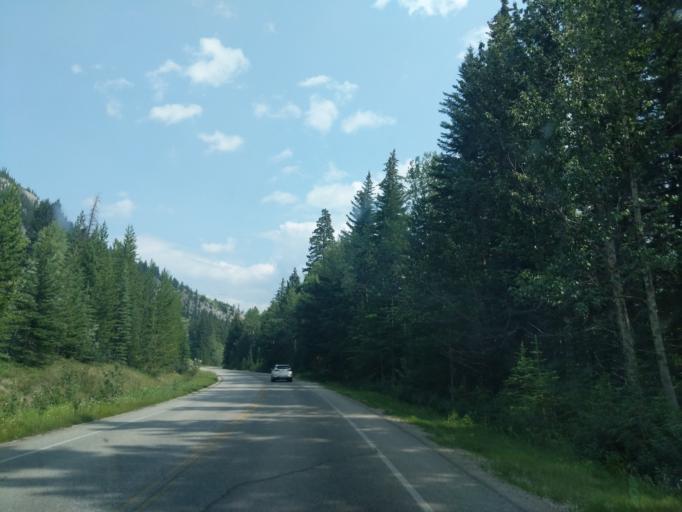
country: CA
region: Alberta
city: Banff
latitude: 51.1723
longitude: -115.7075
